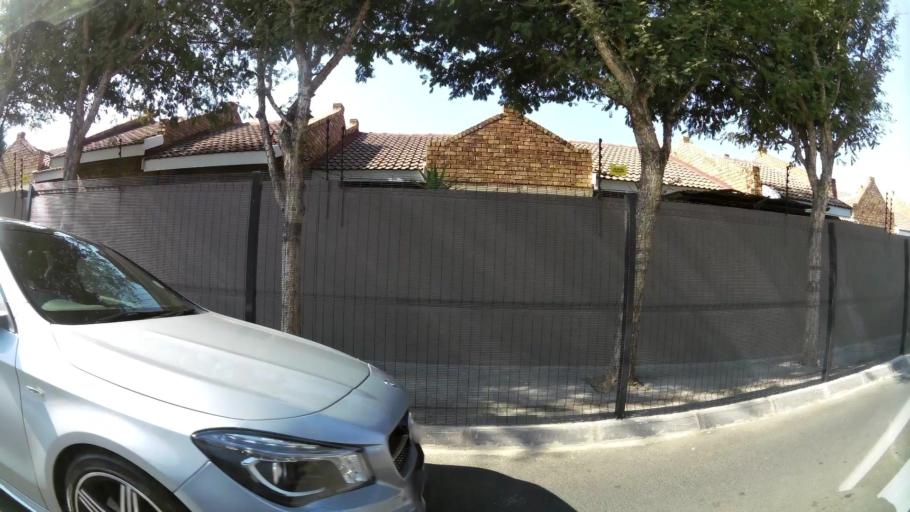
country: ZA
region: Gauteng
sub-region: City of Johannesburg Metropolitan Municipality
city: Modderfontein
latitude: -26.1190
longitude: 28.1545
